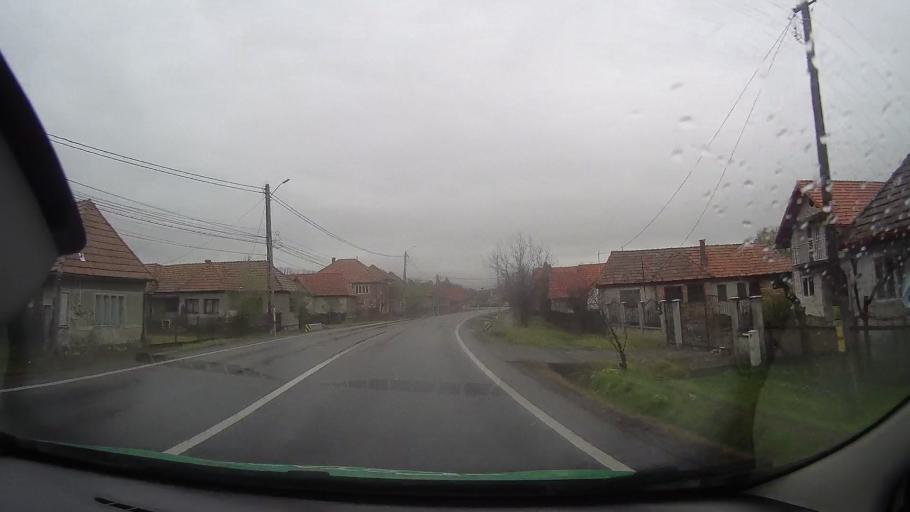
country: RO
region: Mures
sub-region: Comuna Brancovenesti
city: Brancovenesti
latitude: 46.8553
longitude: 24.7572
